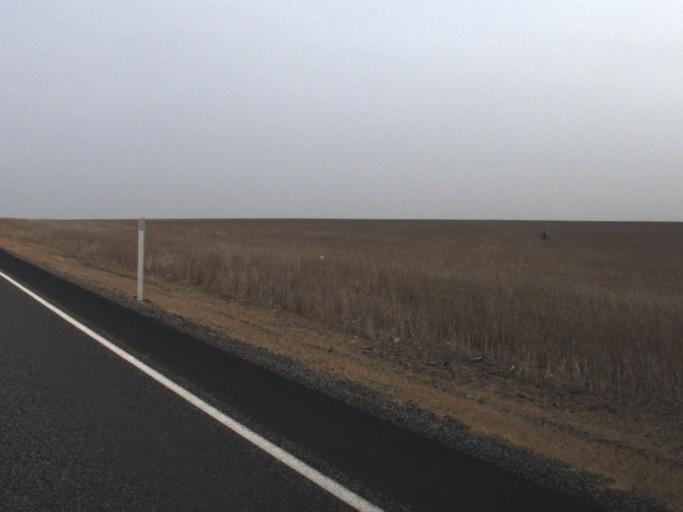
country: US
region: Washington
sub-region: Benton County
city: Prosser
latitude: 46.1871
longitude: -119.6486
